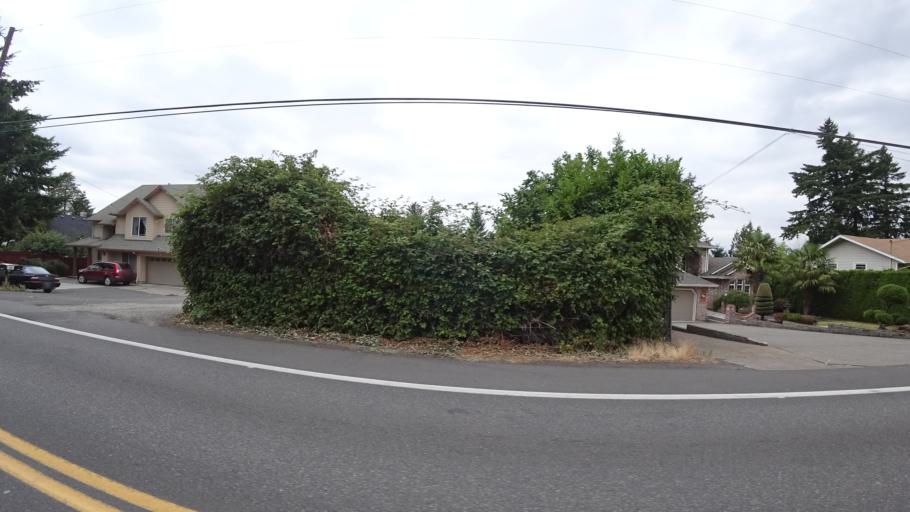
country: US
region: Oregon
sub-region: Multnomah County
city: Lents
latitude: 45.5489
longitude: -122.5486
